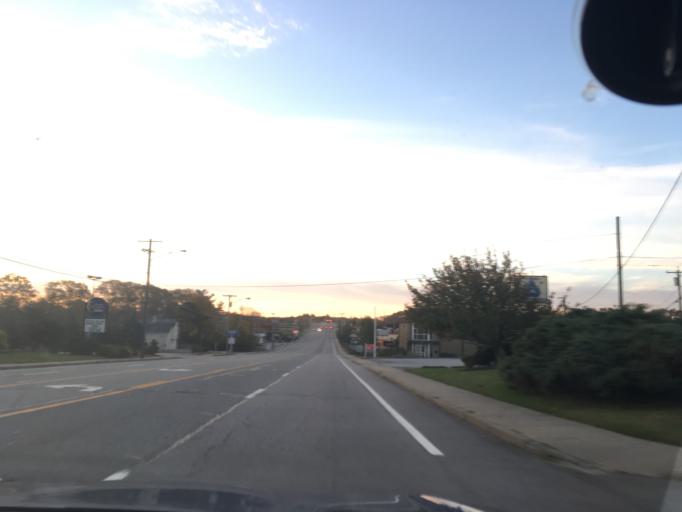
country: US
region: Rhode Island
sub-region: Kent County
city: East Greenwich
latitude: 41.6106
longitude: -71.4571
